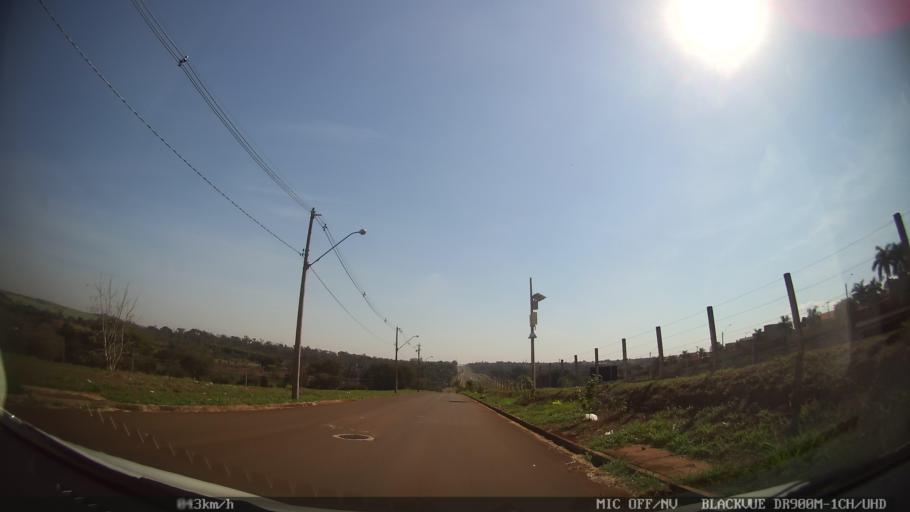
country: BR
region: Sao Paulo
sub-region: Ribeirao Preto
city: Ribeirao Preto
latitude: -21.2185
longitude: -47.8313
